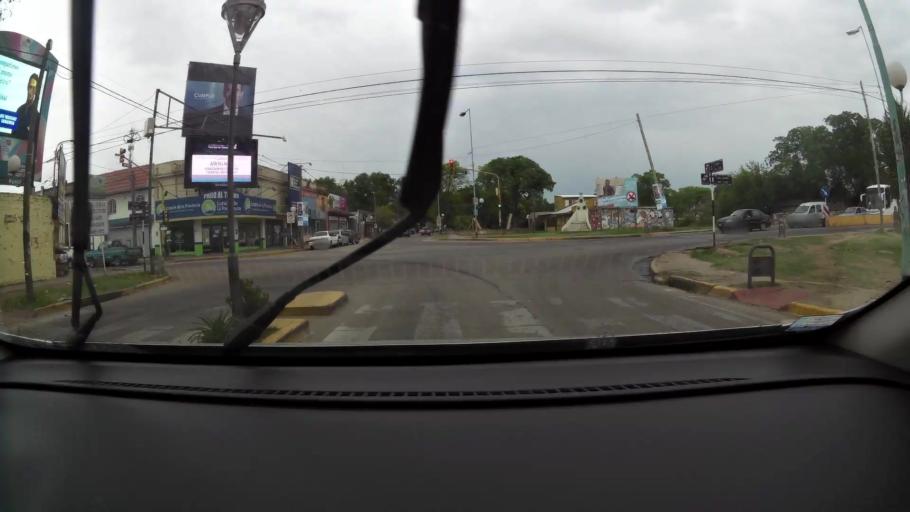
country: AR
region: Buenos Aires
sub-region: Partido de Zarate
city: Zarate
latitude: -34.1047
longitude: -59.0236
